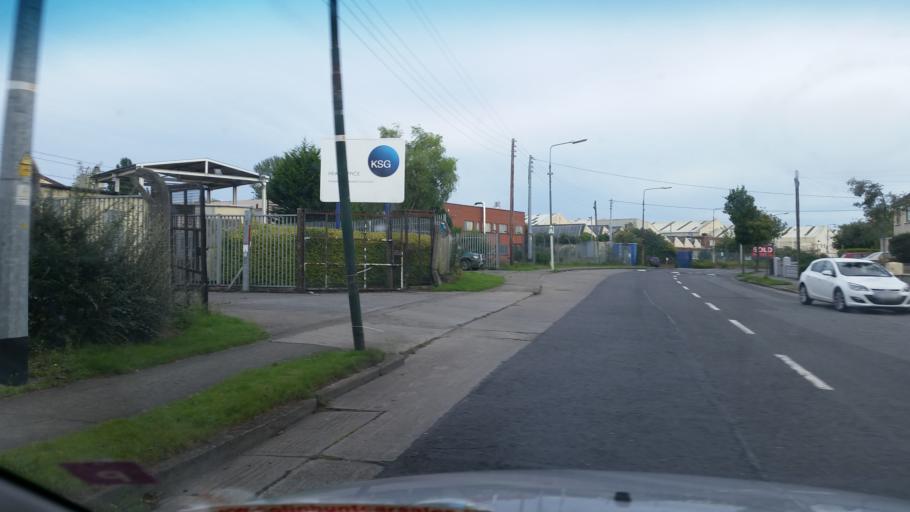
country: IE
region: Leinster
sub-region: Dublin City
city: Finglas
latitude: 53.3961
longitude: -6.3026
